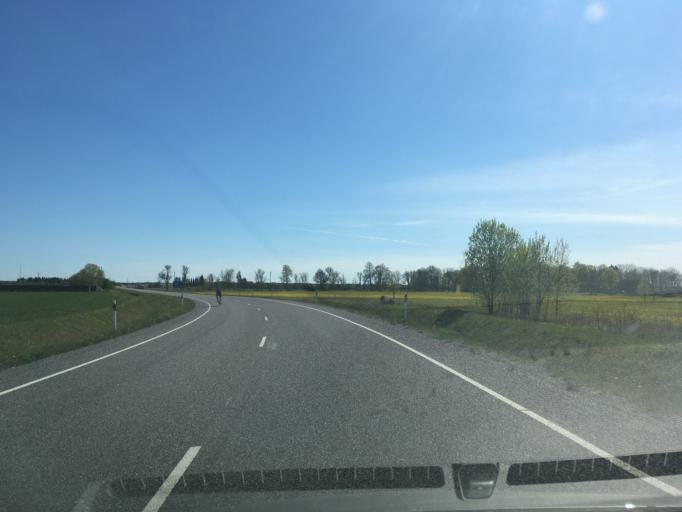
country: EE
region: Harju
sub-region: Rae vald
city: Vaida
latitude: 59.2591
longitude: 25.0184
